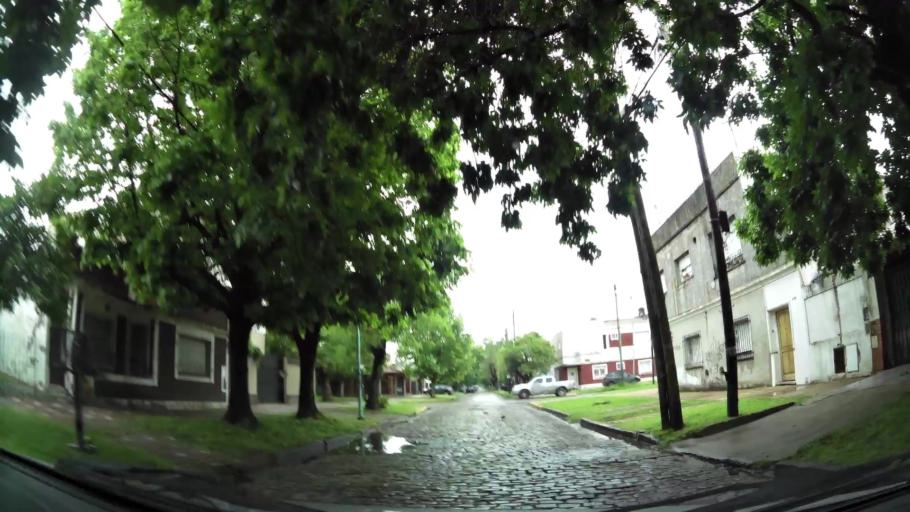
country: AR
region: Buenos Aires
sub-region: Partido de Lomas de Zamora
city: Lomas de Zamora
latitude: -34.7507
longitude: -58.3915
